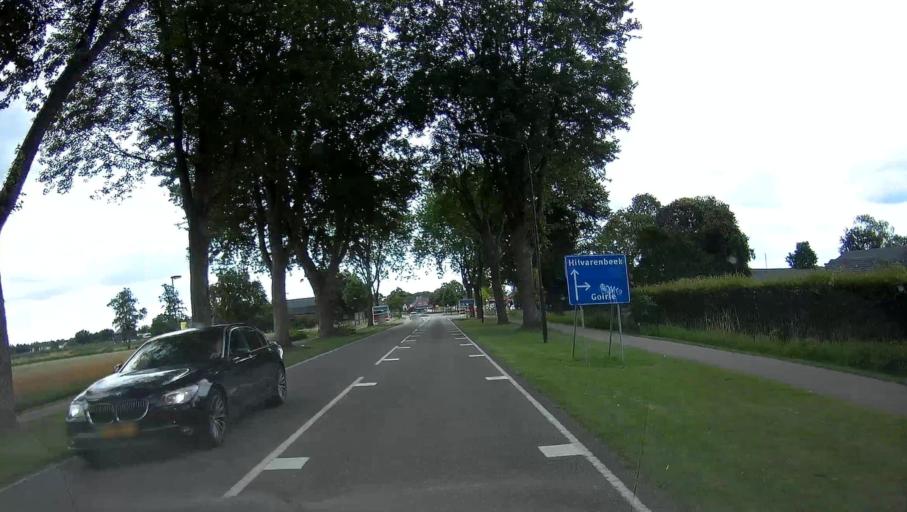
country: NL
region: North Brabant
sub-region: Gemeente Hilvarenbeek
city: Hilvarenbeek
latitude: 51.4989
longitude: 5.1310
